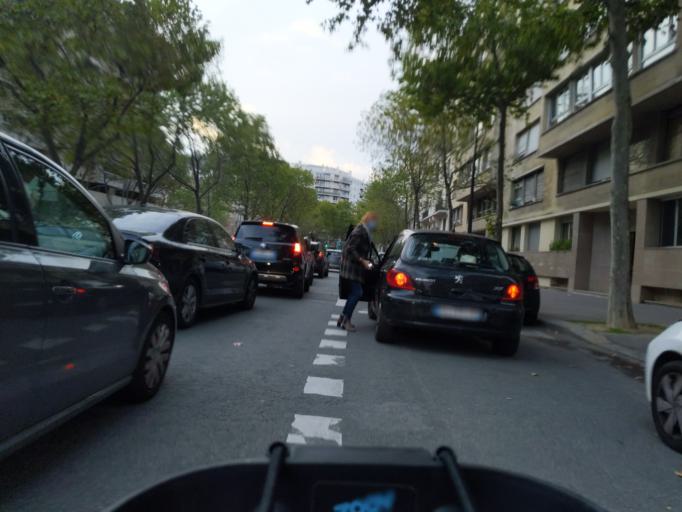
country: FR
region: Ile-de-France
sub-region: Departement des Hauts-de-Seine
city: Boulogne-Billancourt
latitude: 48.8425
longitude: 2.2617
